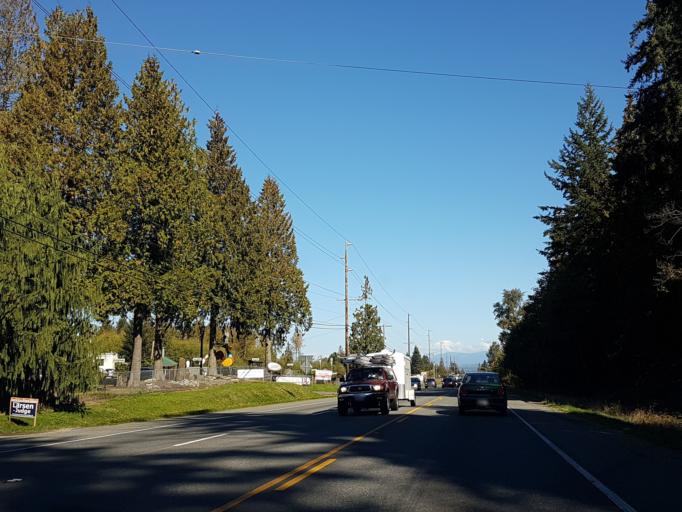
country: US
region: Washington
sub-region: Snohomish County
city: Clearview
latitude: 47.8420
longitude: -122.1213
